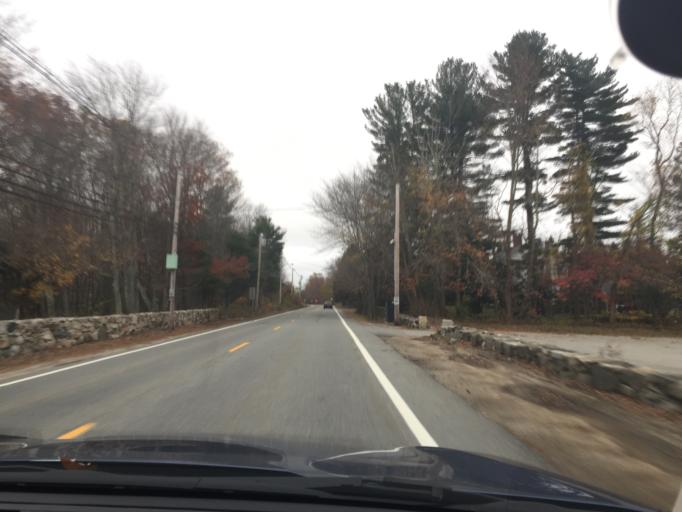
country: US
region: Rhode Island
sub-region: Providence County
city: North Scituate
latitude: 41.8180
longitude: -71.6650
